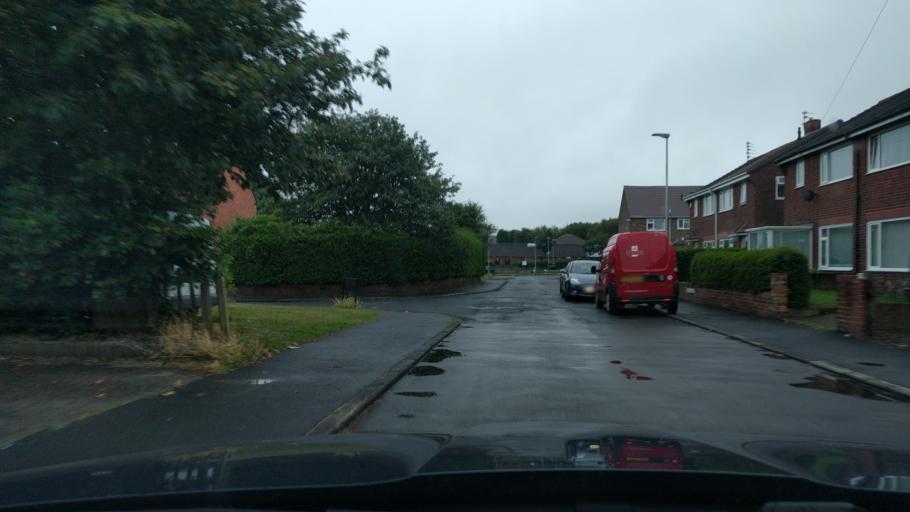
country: GB
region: England
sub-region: Northumberland
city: Bedlington
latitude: 55.1356
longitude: -1.5746
